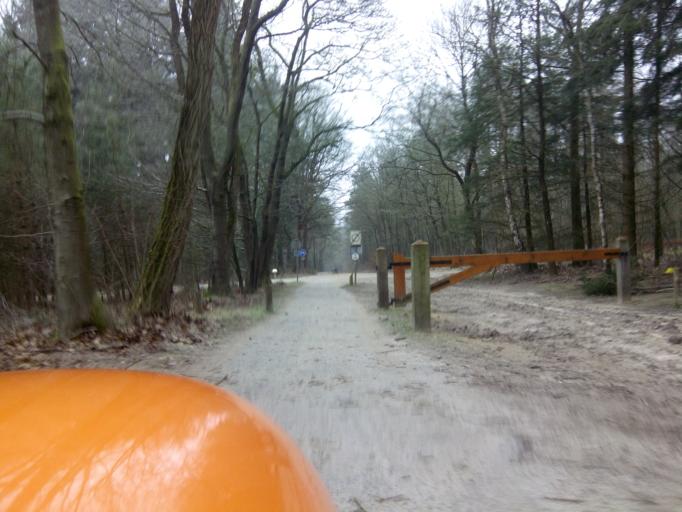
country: NL
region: Gelderland
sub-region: Gemeente Barneveld
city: Stroe
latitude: 52.2154
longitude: 5.6634
